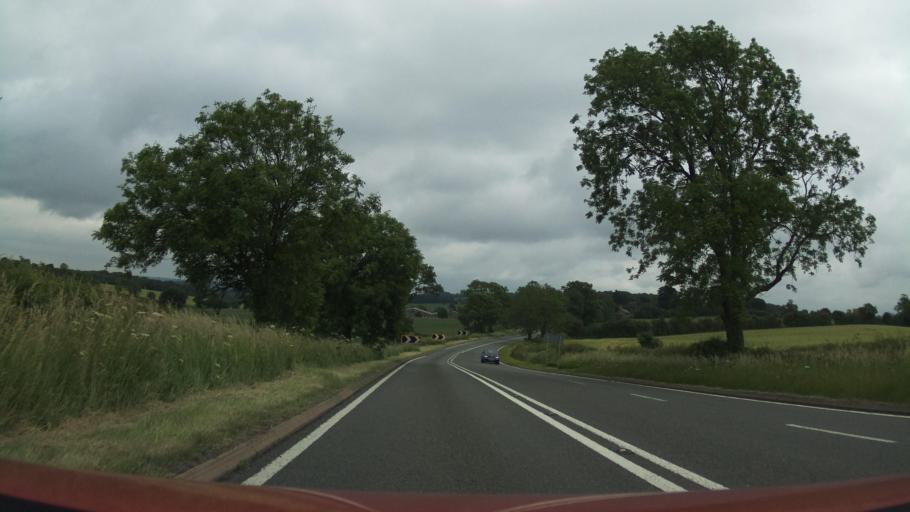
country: GB
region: England
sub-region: Leicestershire
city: Houghton on the Hill
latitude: 52.6070
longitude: -0.8813
